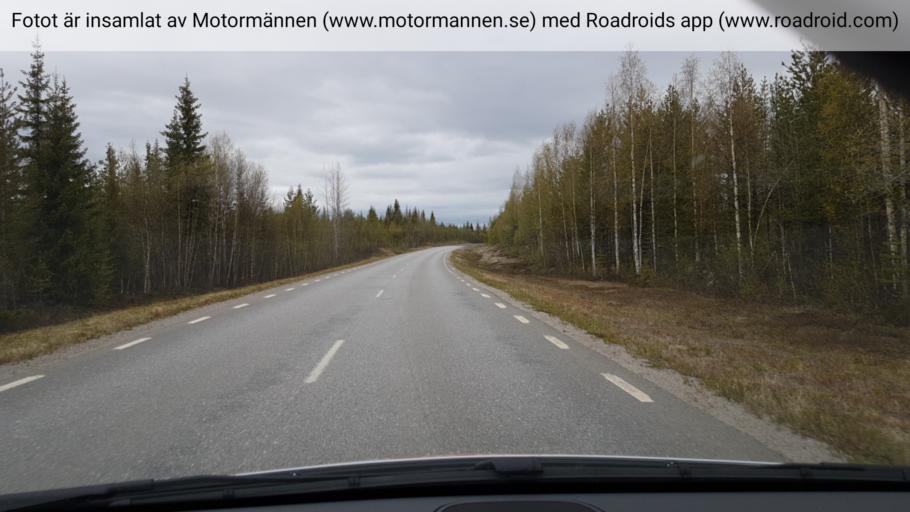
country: SE
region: Vaesterbotten
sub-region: Sorsele Kommun
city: Sorsele
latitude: 65.5147
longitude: 17.3206
